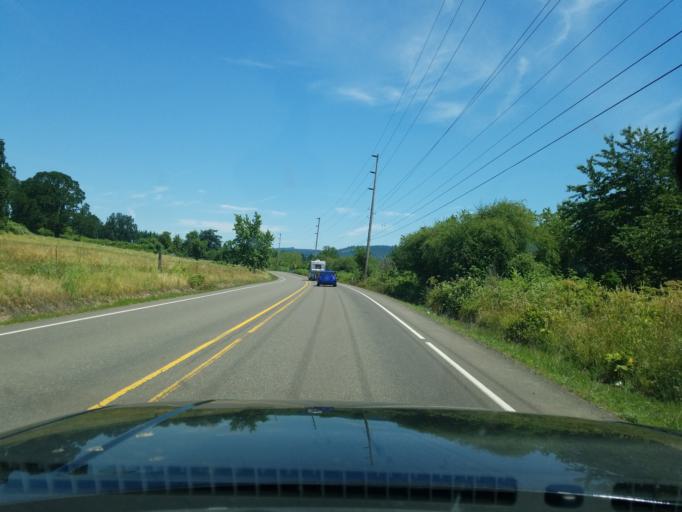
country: US
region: Oregon
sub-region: Yamhill County
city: Yamhill
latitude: 45.4007
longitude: -123.1251
